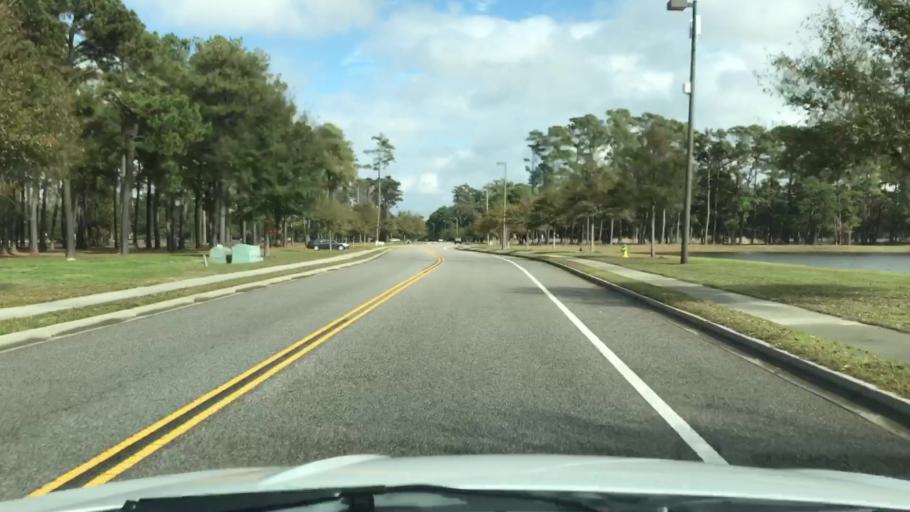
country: US
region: South Carolina
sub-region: Horry County
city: Myrtle Beach
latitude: 33.7218
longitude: -78.8772
